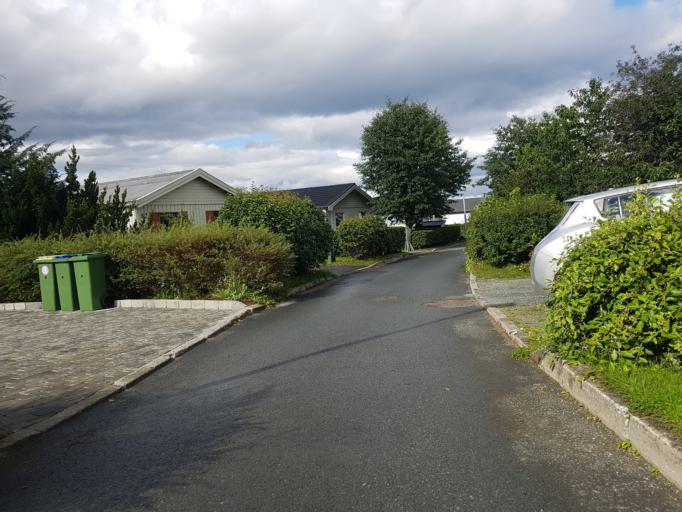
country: NO
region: Sor-Trondelag
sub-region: Trondheim
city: Trondheim
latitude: 63.4146
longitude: 10.4586
